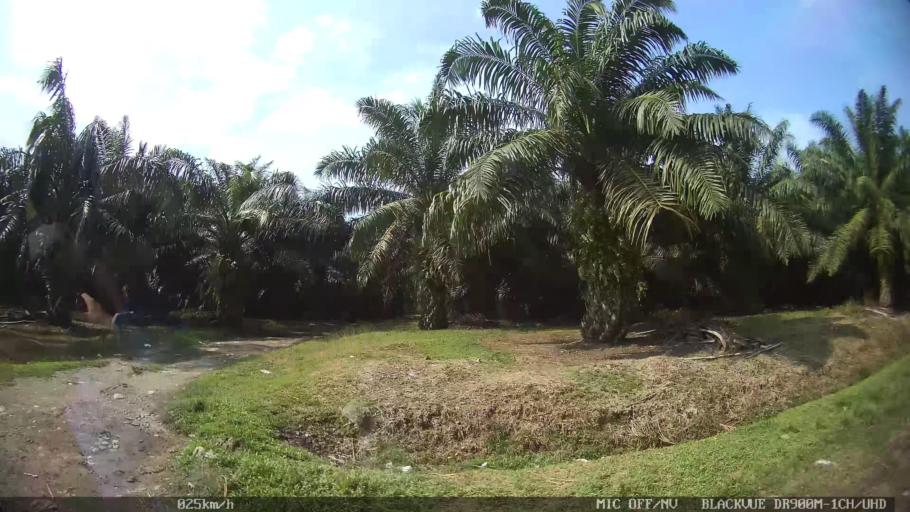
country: ID
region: North Sumatra
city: Binjai
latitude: 3.6428
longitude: 98.5223
